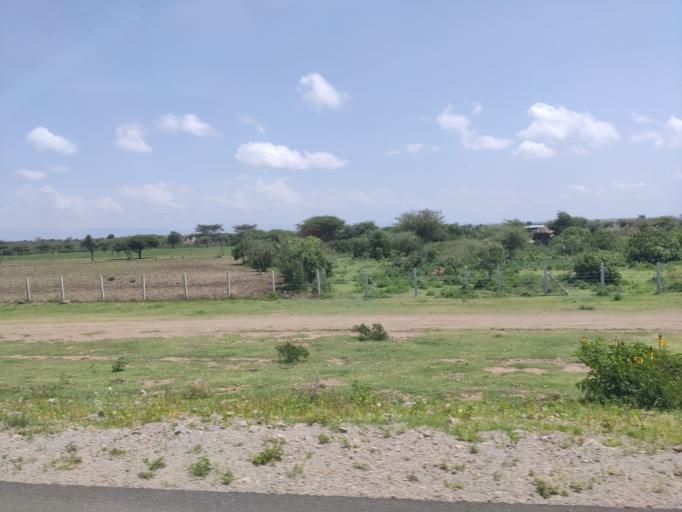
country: ET
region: Oromiya
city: Ziway
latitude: 8.2591
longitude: 38.8979
